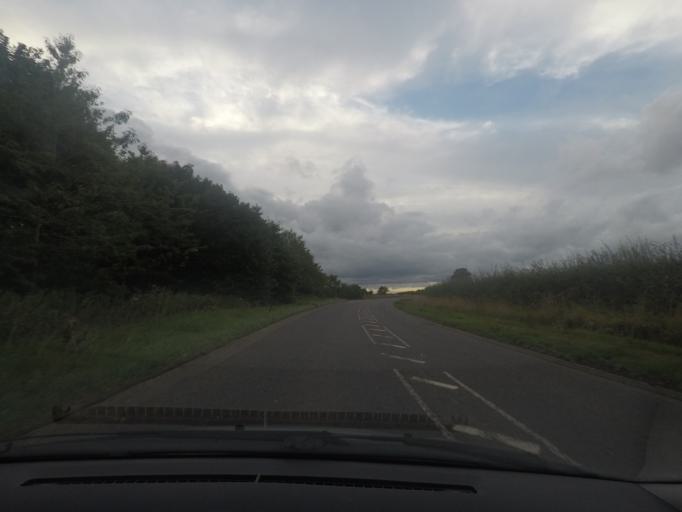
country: GB
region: England
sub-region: Lincolnshire
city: Burwell
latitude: 53.2696
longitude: 0.0728
